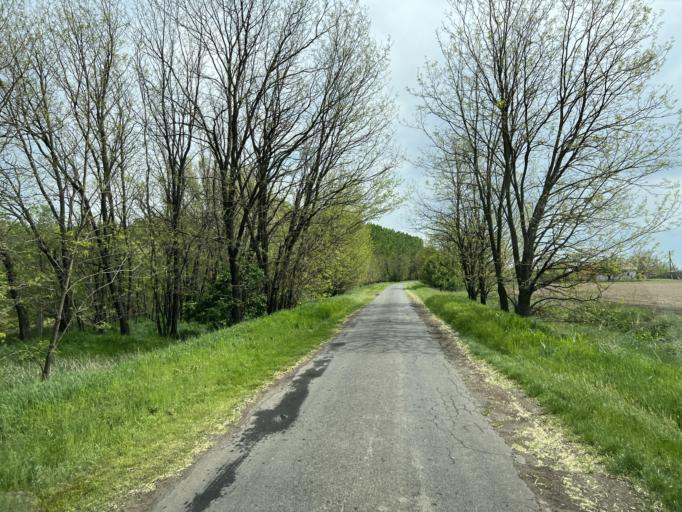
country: HU
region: Pest
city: Nagykoros
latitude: 46.9773
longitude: 19.8125
